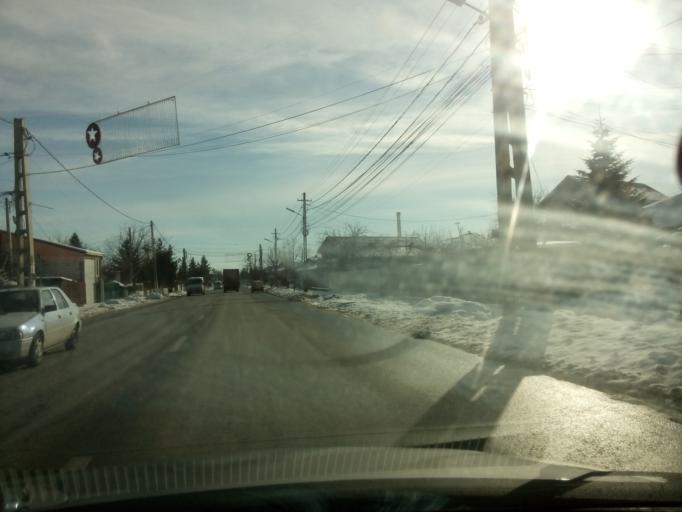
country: RO
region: Ilfov
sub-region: Comuna Popesti-Leordeni
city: Popesti-Leordeni
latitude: 44.3761
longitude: 26.1748
